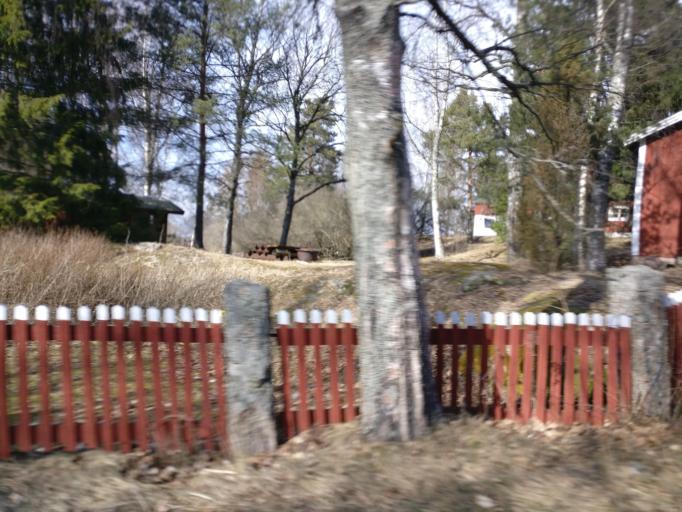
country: FI
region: Varsinais-Suomi
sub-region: Salo
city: Suomusjaervi
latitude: 60.3164
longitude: 23.7127
